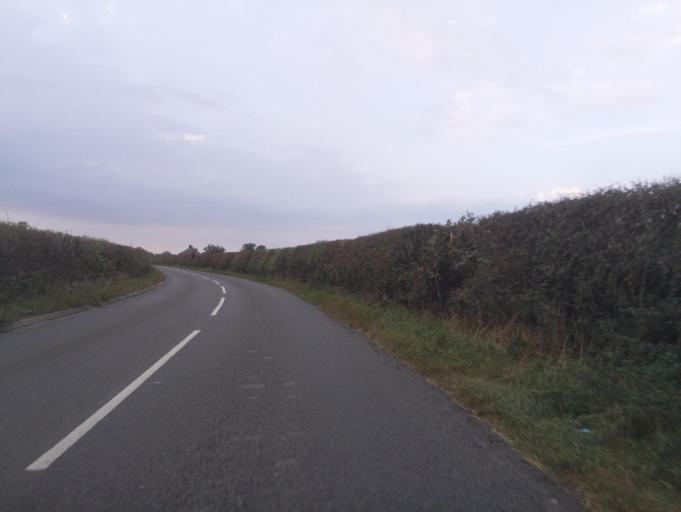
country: GB
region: England
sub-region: Lincolnshire
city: Skellingthorpe
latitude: 53.1377
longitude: -0.6450
